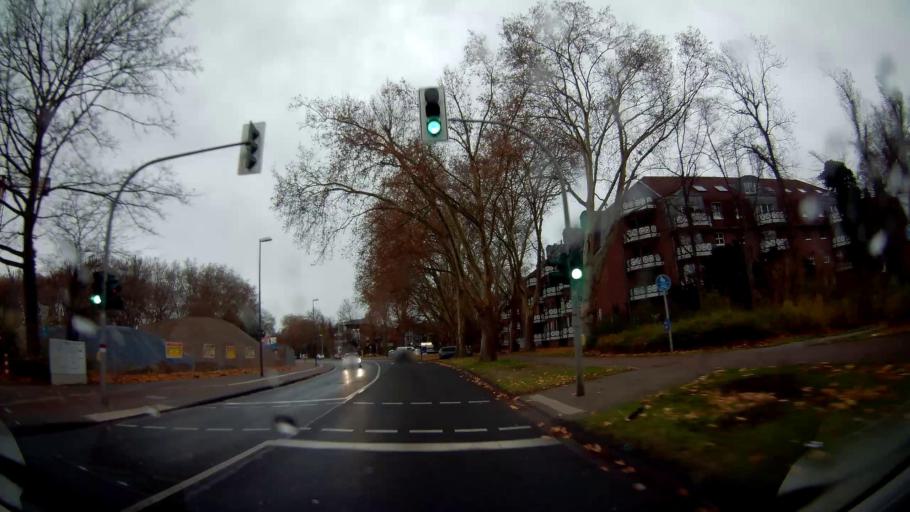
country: DE
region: North Rhine-Westphalia
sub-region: Regierungsbezirk Munster
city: Gelsenkirchen
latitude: 51.5042
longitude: 7.0796
